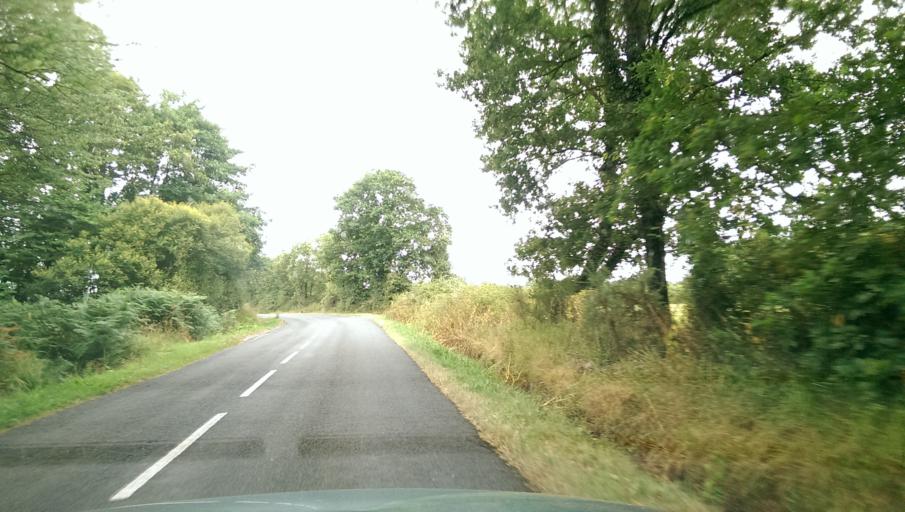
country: FR
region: Pays de la Loire
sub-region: Departement de la Loire-Atlantique
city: La Planche
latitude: 47.0013
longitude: -1.3974
